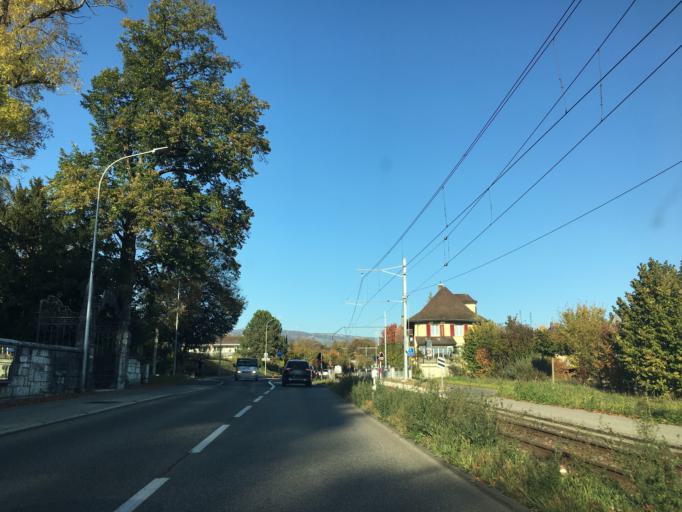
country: CH
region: Solothurn
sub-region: Bezirk Solothurn
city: Solothurn
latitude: 47.2184
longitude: 7.5525
